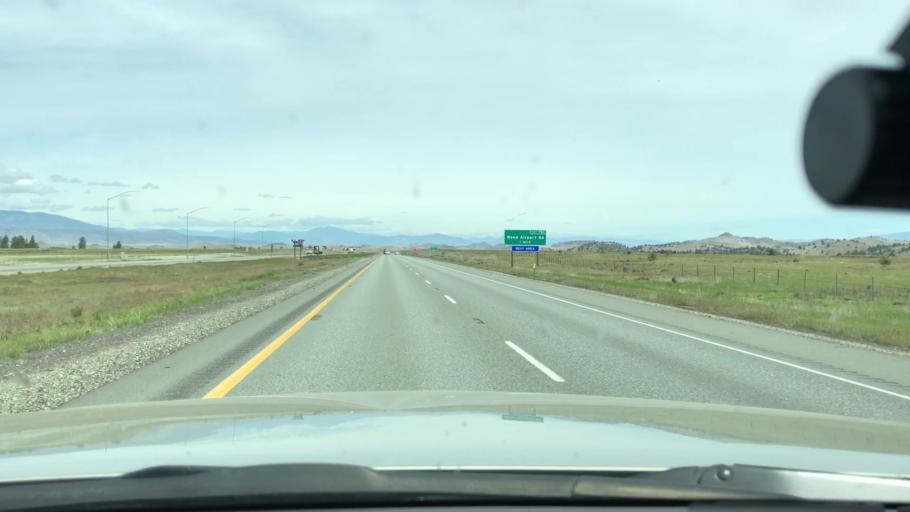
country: US
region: California
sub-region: Siskiyou County
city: Weed
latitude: 41.4576
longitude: -122.4449
